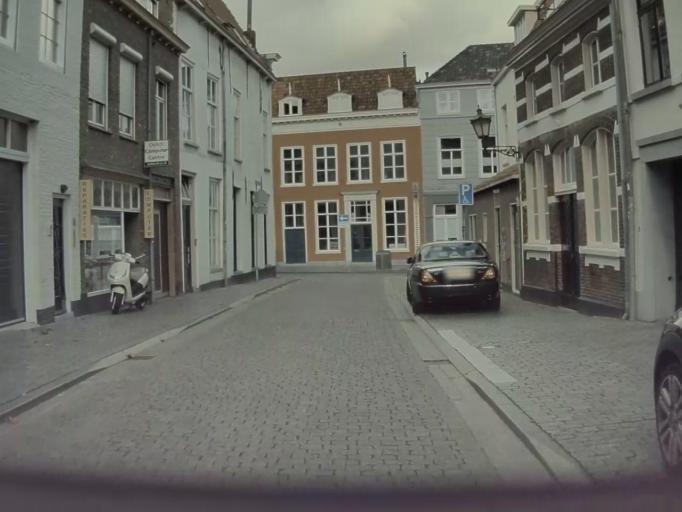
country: NL
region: North Brabant
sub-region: Gemeente Bergen op Zoom
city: Bergen op Zoom
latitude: 51.4948
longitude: 4.2847
